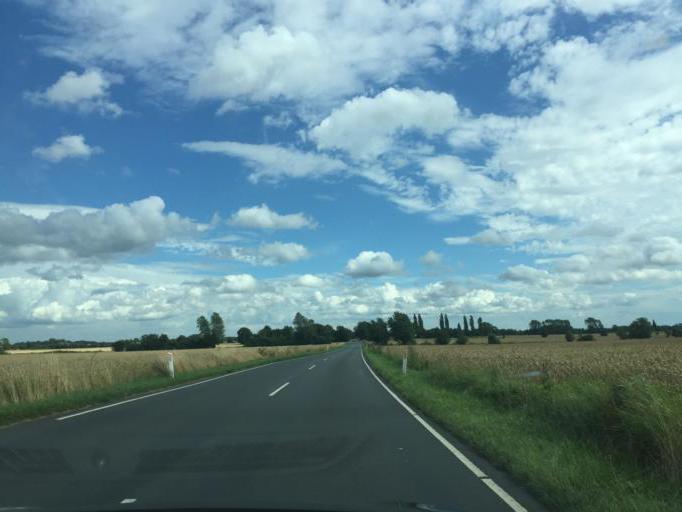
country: DK
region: South Denmark
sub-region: Nordfyns Kommune
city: Otterup
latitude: 55.4854
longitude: 10.3660
